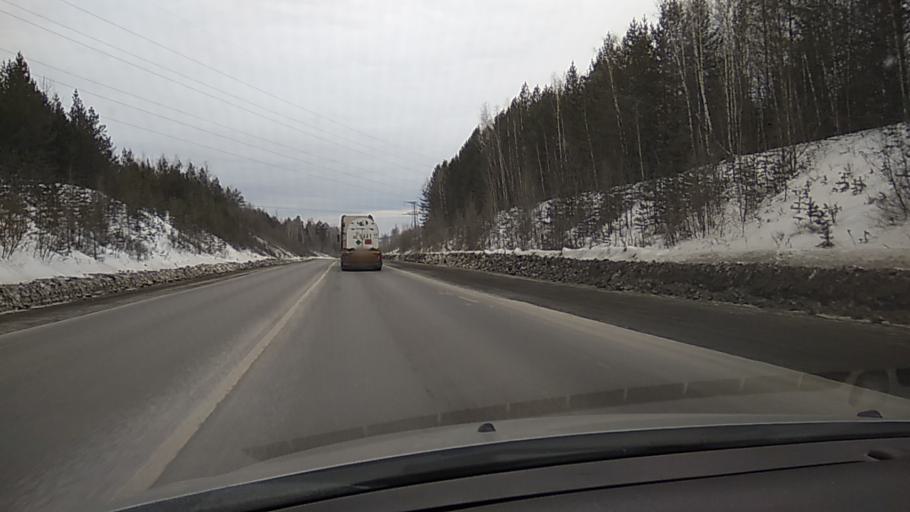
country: RU
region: Sverdlovsk
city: Talitsa
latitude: 56.8325
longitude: 59.9967
